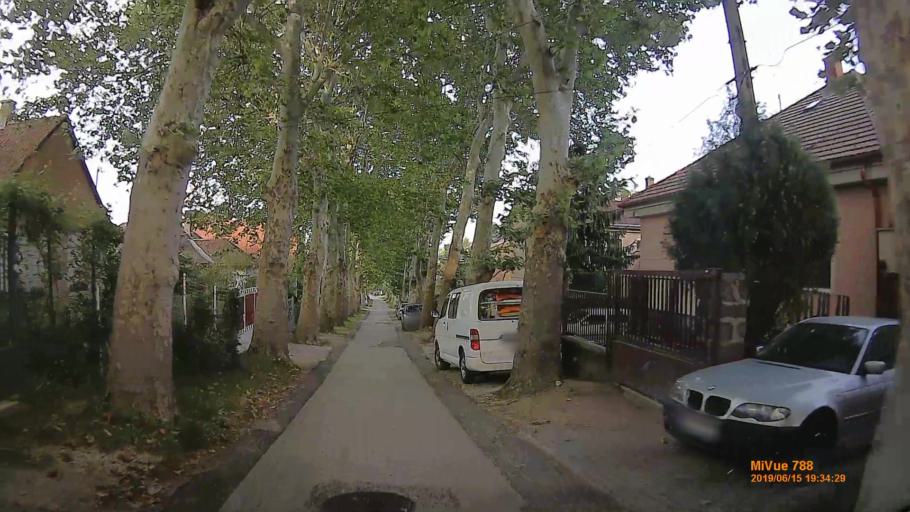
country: HU
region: Veszprem
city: Balatonalmadi
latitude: 47.0189
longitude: 18.0021
